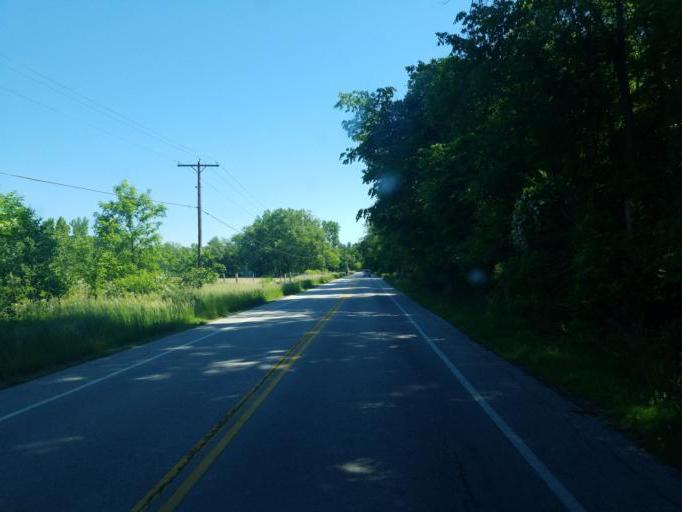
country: US
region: Ohio
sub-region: Summit County
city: Peninsula
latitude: 41.1864
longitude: -81.5746
